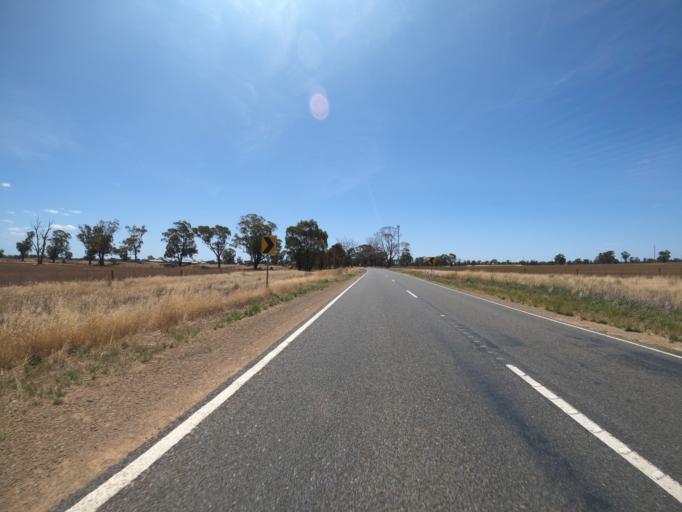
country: AU
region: Victoria
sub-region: Moira
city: Yarrawonga
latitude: -36.1907
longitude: 145.9671
